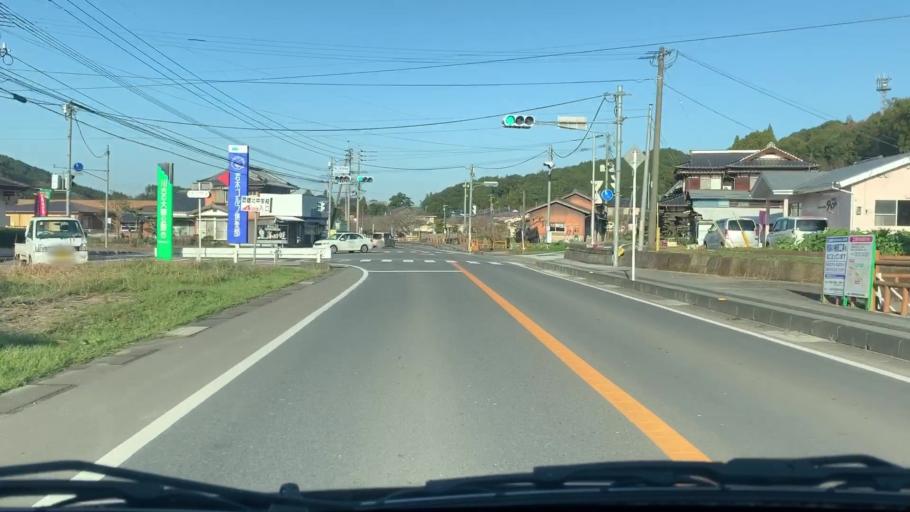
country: JP
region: Saga Prefecture
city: Takeocho-takeo
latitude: 33.2539
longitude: 129.9921
